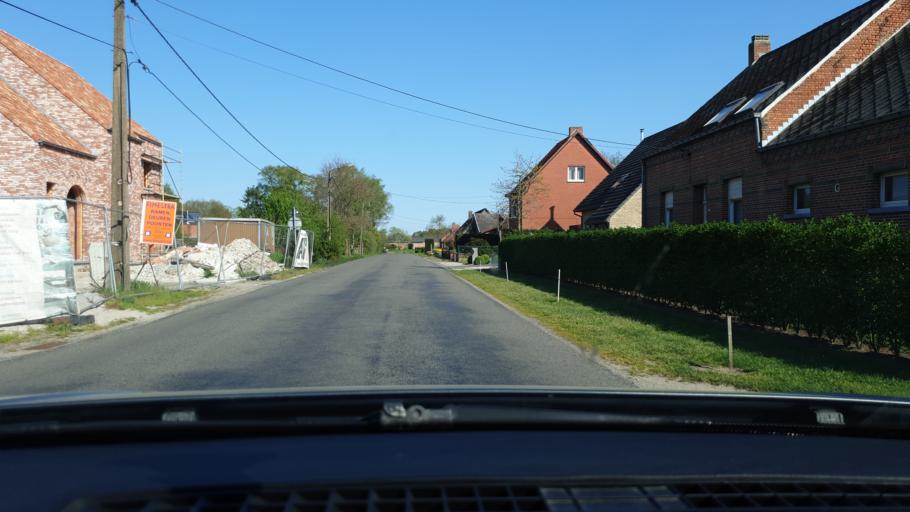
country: BE
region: Flanders
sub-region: Provincie Antwerpen
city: Geel
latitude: 51.1805
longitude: 4.9332
